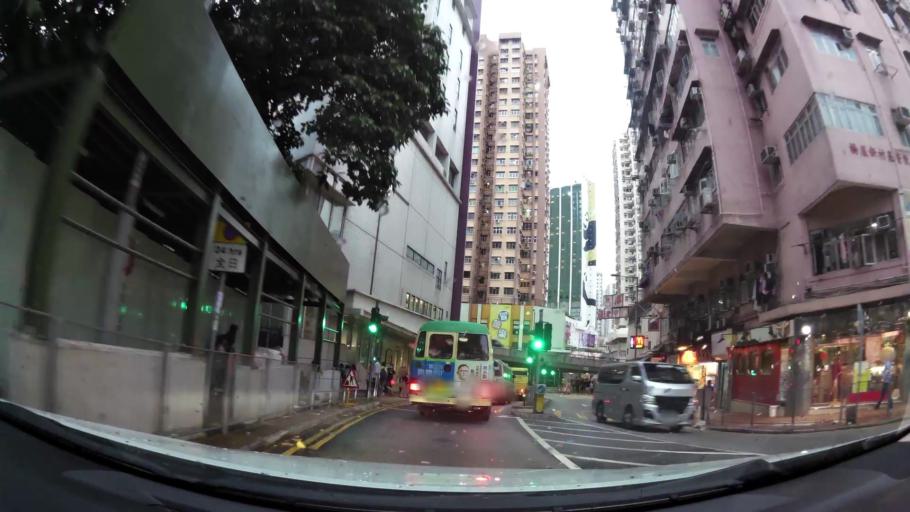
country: HK
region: Tsuen Wan
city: Tsuen Wan
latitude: 22.3680
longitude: 114.1227
